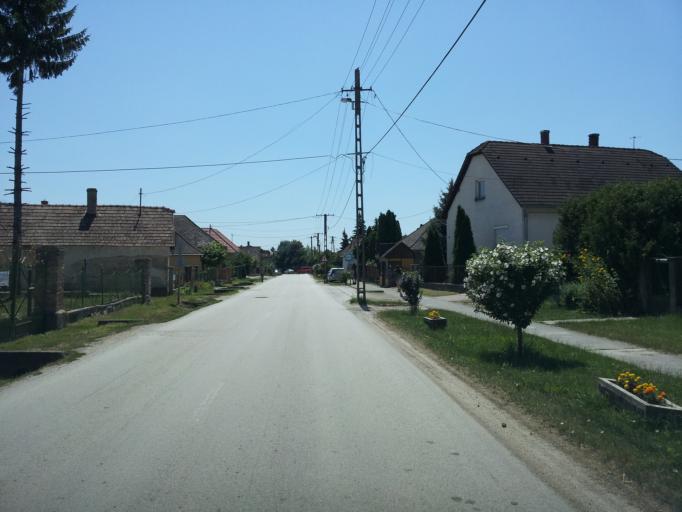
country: HU
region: Veszprem
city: Balatonkenese
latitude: 47.0467
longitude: 18.1848
